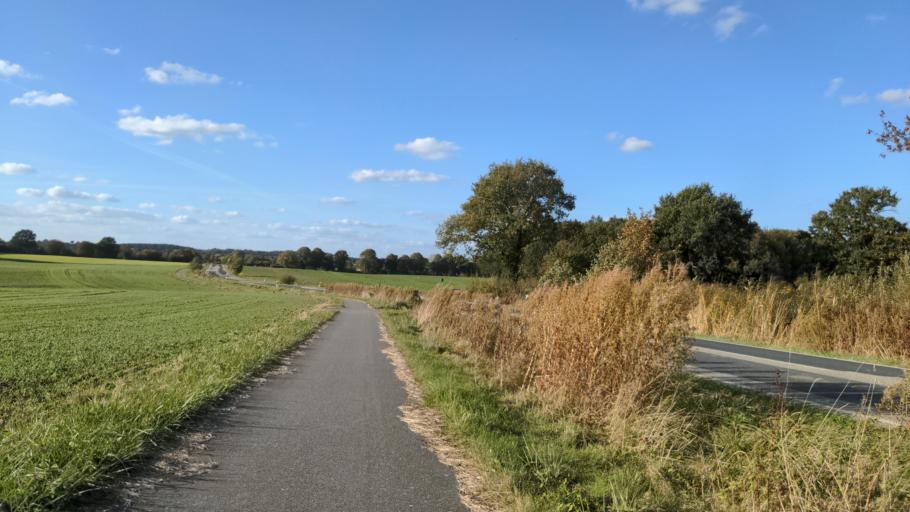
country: DE
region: Schleswig-Holstein
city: Zarpen
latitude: 53.8621
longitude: 10.5340
